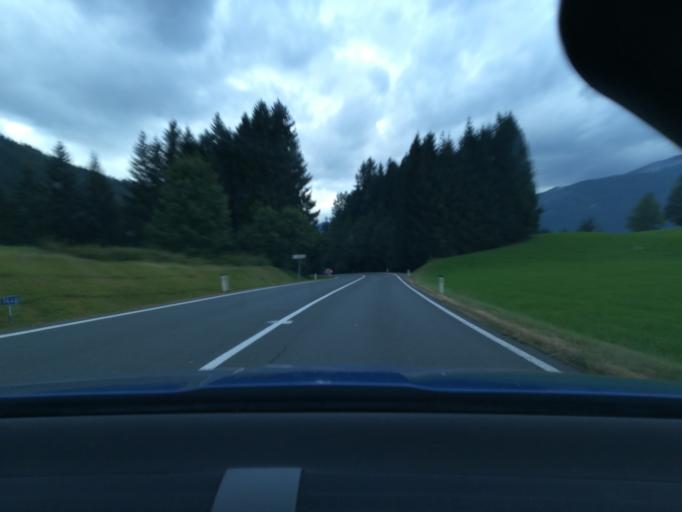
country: AT
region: Salzburg
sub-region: Politischer Bezirk Hallein
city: Abtenau
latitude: 47.5800
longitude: 13.3223
